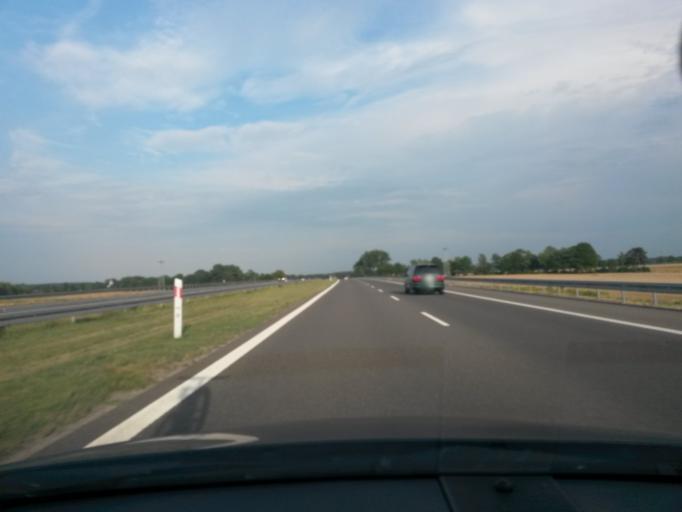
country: PL
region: Lodz Voivodeship
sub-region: Powiat zgierski
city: Zgierz
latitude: 51.9000
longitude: 19.4678
